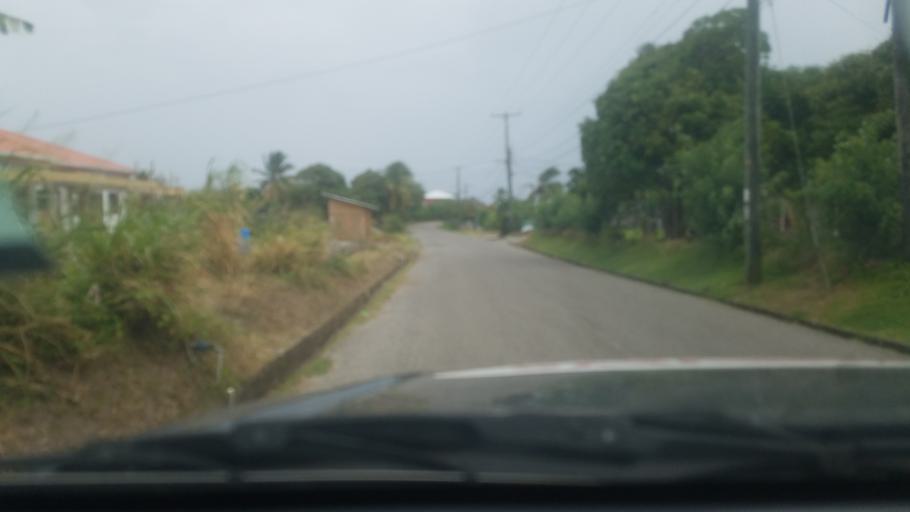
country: LC
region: Laborie Quarter
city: Laborie
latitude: 13.7507
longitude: -60.9805
